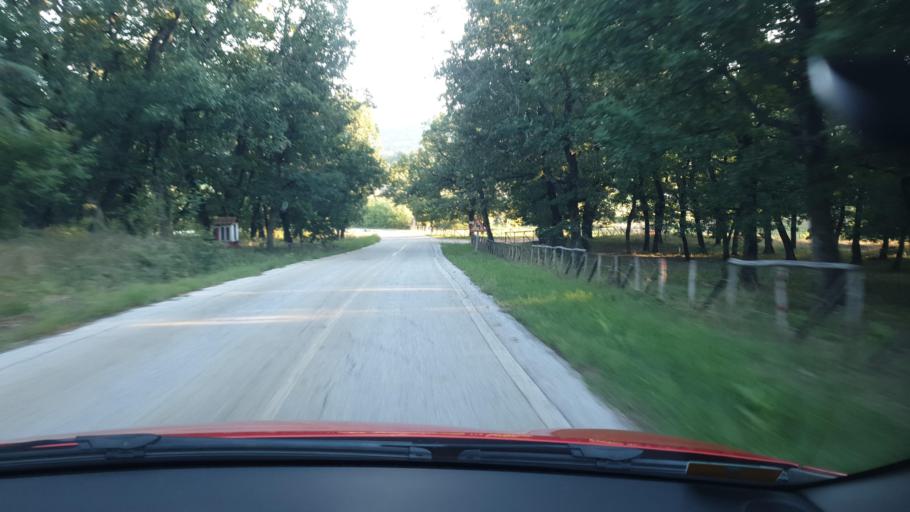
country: GR
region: Central Macedonia
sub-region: Nomos Chalkidikis
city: Galatista
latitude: 40.5242
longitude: 23.2781
